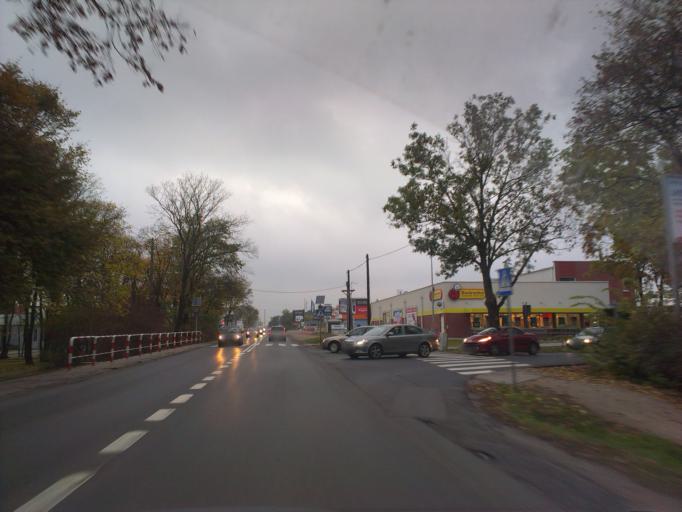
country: PL
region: Greater Poland Voivodeship
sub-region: Powiat poznanski
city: Suchy Las
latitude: 52.4585
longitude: 16.8958
